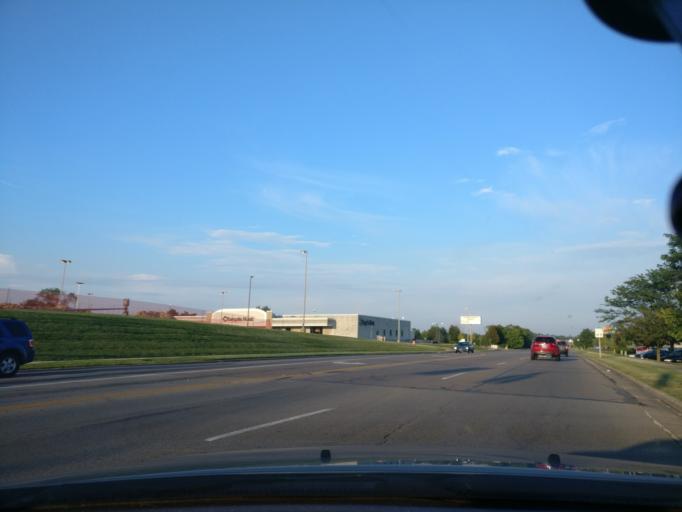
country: US
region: Ohio
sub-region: Montgomery County
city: West Carrollton City
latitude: 39.6282
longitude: -84.2258
